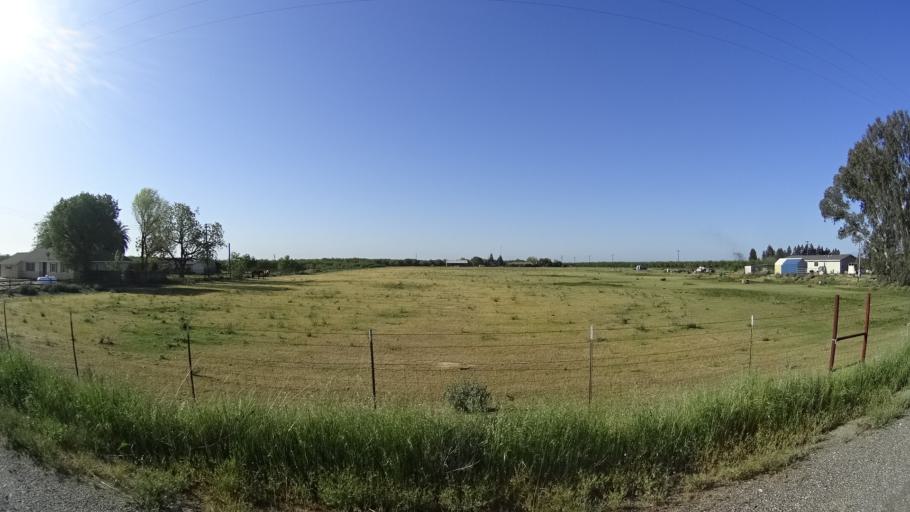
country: US
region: California
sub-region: Glenn County
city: Orland
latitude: 39.6816
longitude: -122.1390
